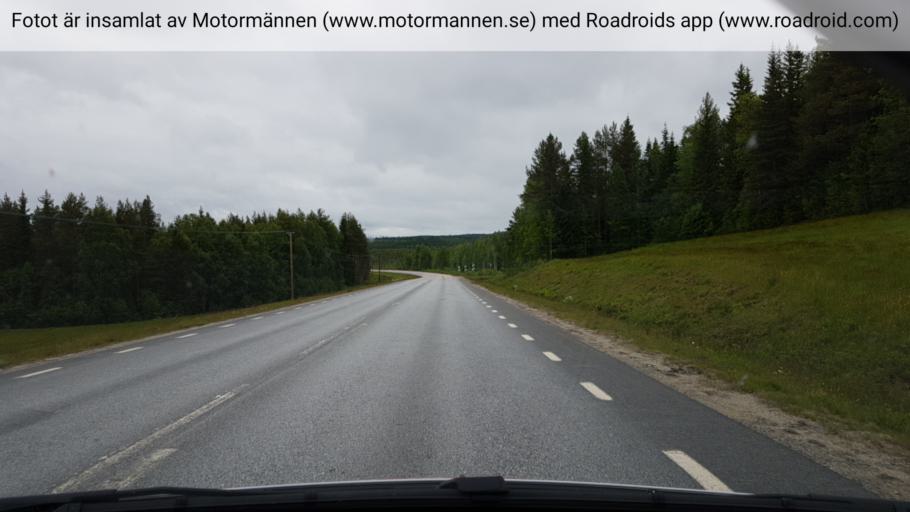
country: SE
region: Vaesterbotten
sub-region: Vannas Kommun
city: Vaennaes
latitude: 64.0362
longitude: 19.6909
